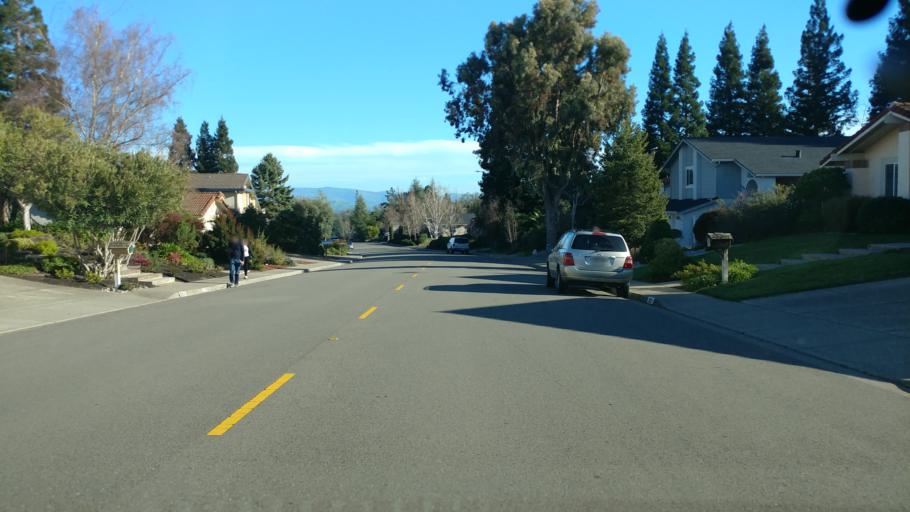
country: US
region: California
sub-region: Contra Costa County
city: San Ramon
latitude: 37.7528
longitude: -121.9676
